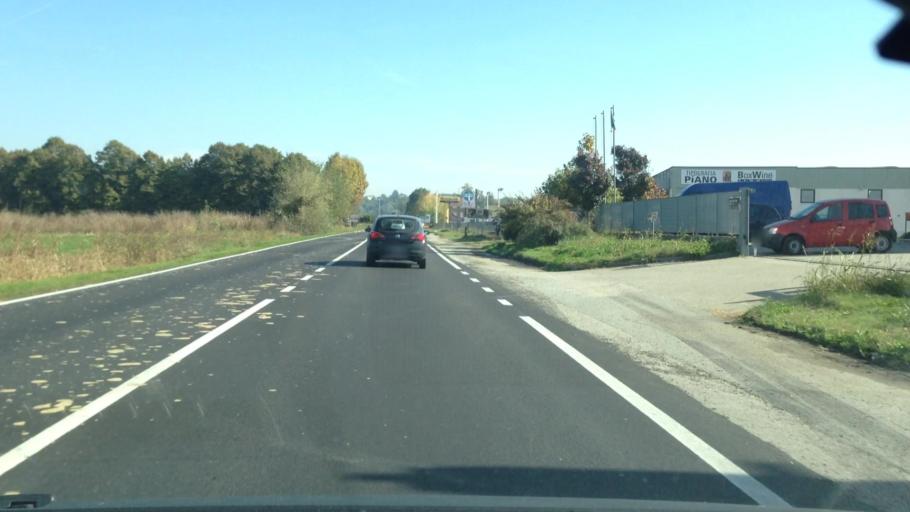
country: IT
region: Piedmont
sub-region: Provincia di Asti
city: Azzano d'Asti
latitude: 44.9068
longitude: 8.2652
